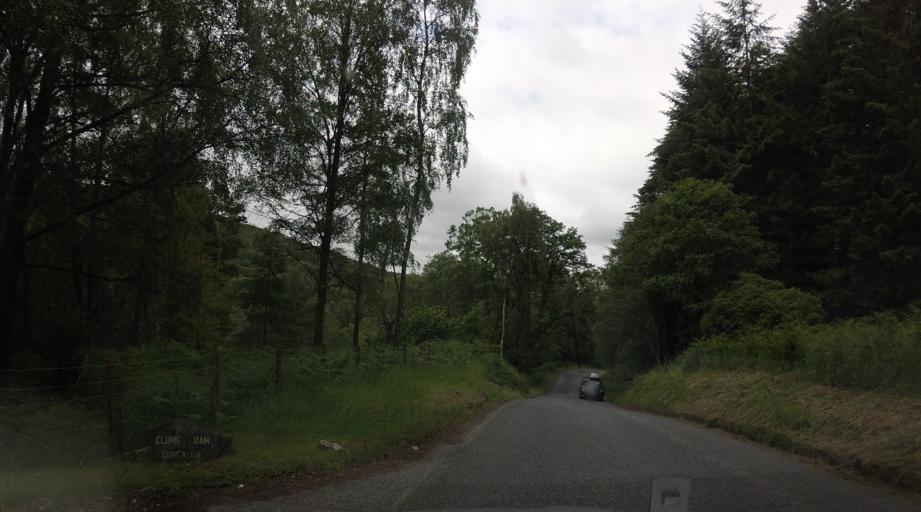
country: GB
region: Scotland
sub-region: Perth and Kinross
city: Pitlochry
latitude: 56.7208
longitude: -3.8285
